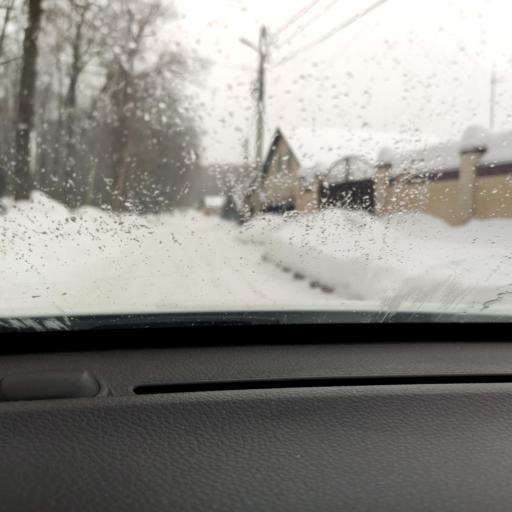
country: RU
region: Tatarstan
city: Stolbishchi
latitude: 55.6724
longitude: 49.1121
